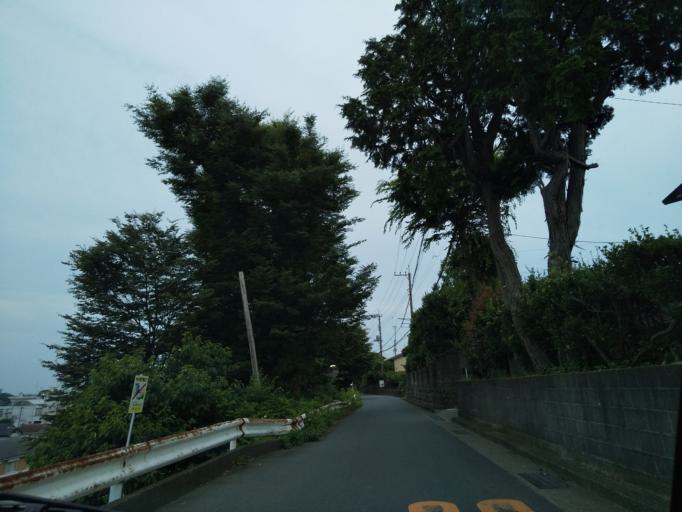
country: JP
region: Kanagawa
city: Atsugi
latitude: 35.4748
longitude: 139.3521
